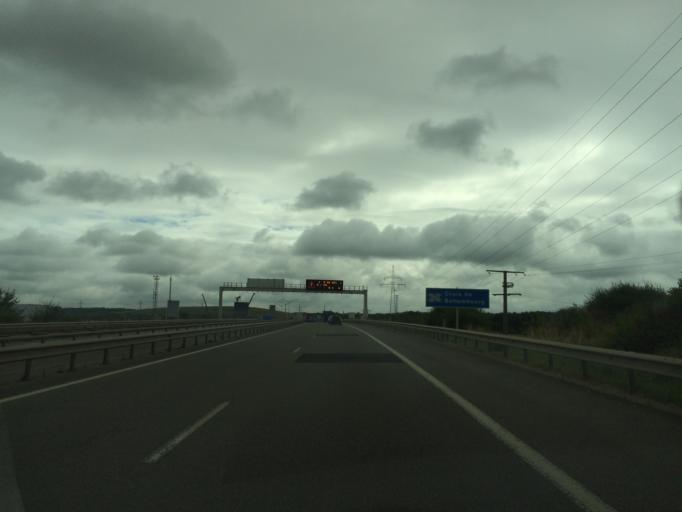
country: LU
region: Luxembourg
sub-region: Canton d'Esch-sur-Alzette
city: Bettembourg
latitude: 49.4970
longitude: 6.1021
